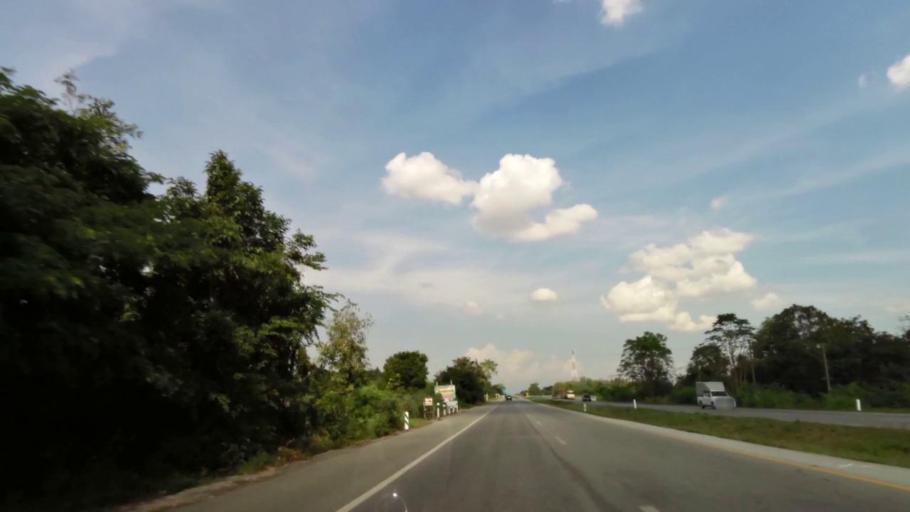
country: TH
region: Uttaradit
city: Thong Saen Khan
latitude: 17.4612
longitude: 100.2375
